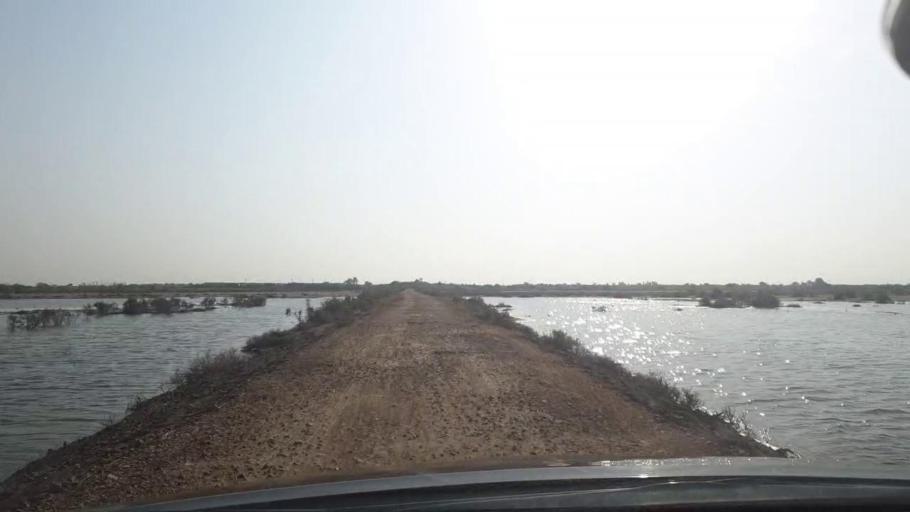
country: PK
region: Sindh
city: Tando Bago
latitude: 24.6510
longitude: 69.1327
